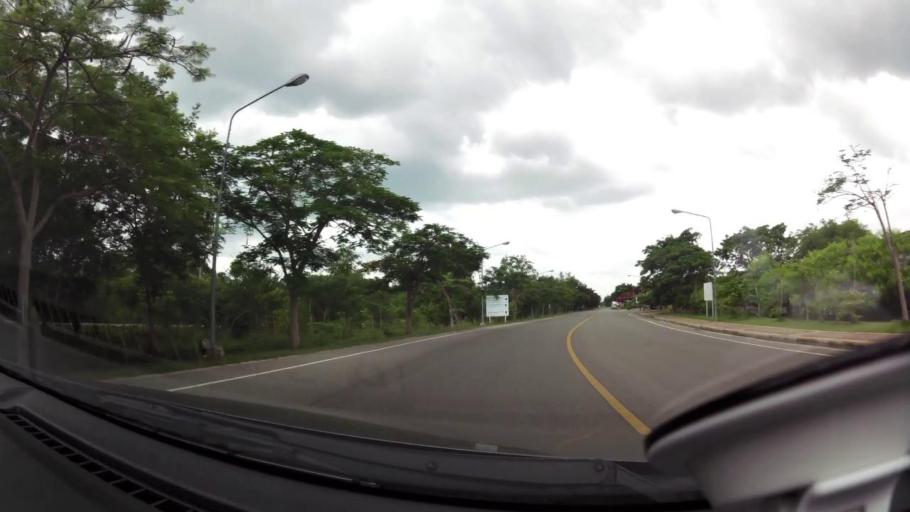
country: TH
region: Phetchaburi
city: Cha-am
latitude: 12.7047
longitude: 99.9586
